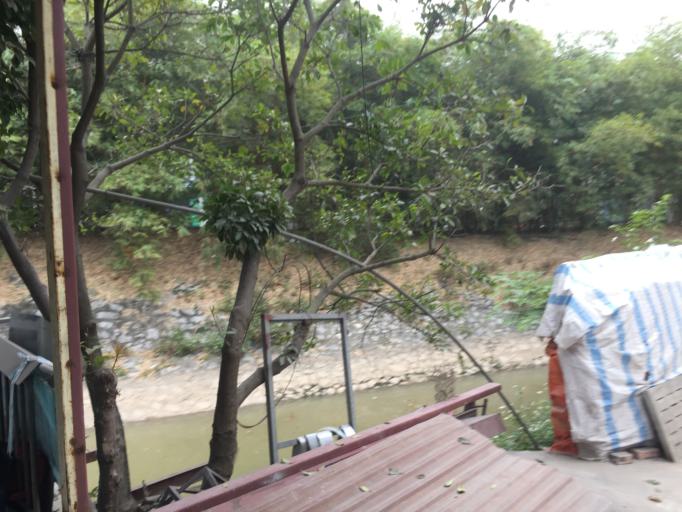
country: VN
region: Hung Yen
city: Van Giang
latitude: 20.9706
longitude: 105.9225
